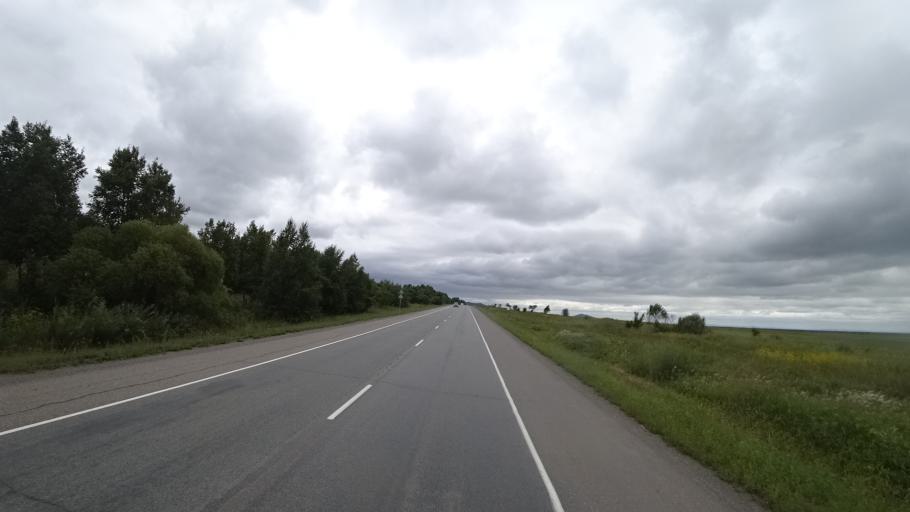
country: RU
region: Primorskiy
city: Chernigovka
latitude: 44.3080
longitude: 132.5414
